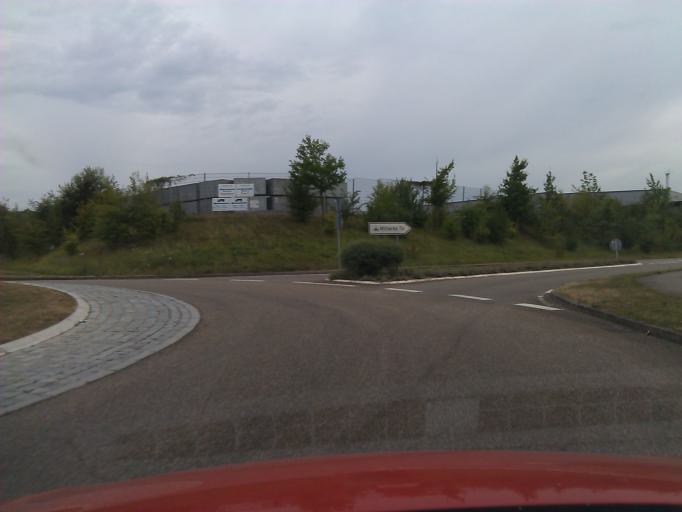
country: DE
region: Baden-Wuerttemberg
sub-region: Regierungsbezirk Stuttgart
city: Guglingen
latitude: 49.0612
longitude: 8.9978
